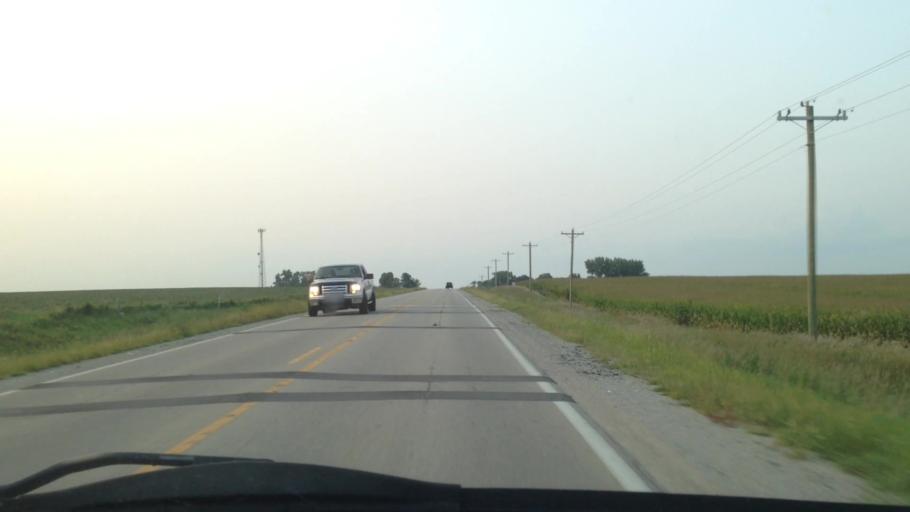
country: US
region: Iowa
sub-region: Linn County
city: Palo
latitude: 42.0733
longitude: -91.8691
